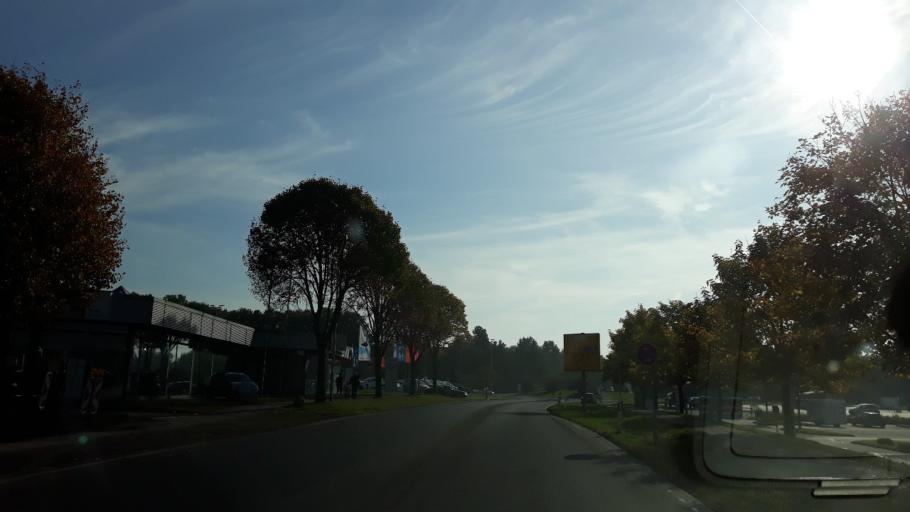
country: DE
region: Schleswig-Holstein
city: Schleswig
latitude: 54.5320
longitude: 9.5743
